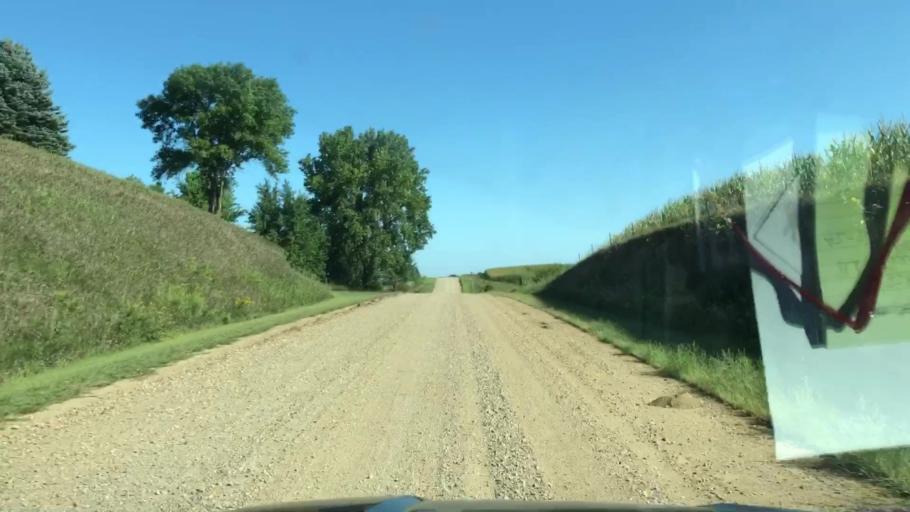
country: US
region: Iowa
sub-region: Woodbury County
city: Sergeant Bluff
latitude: 42.4694
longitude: -96.2921
